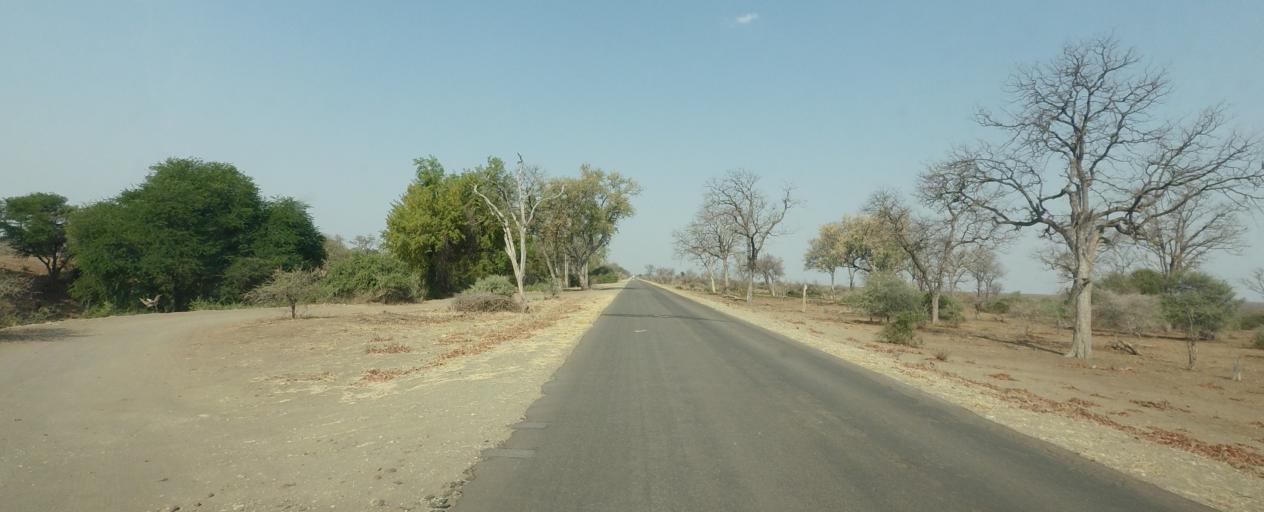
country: ZA
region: Limpopo
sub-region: Mopani District Municipality
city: Giyani
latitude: -23.0967
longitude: 31.3939
